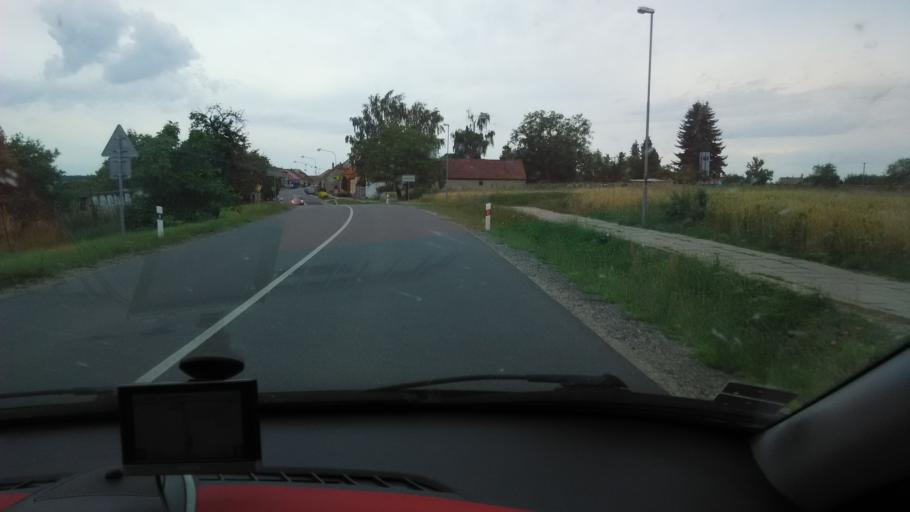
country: CZ
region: South Moravian
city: Kostice
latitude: 48.7523
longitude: 16.9850
